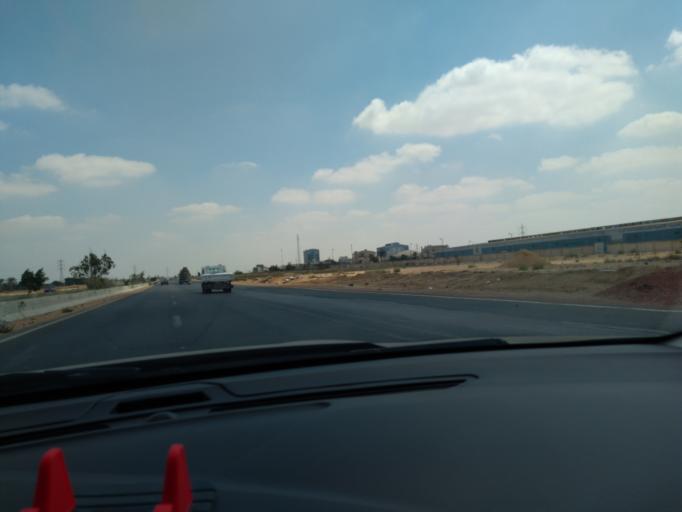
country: EG
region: Al Isma'iliyah
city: At Tall al Kabir
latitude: 30.3392
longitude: 31.8638
